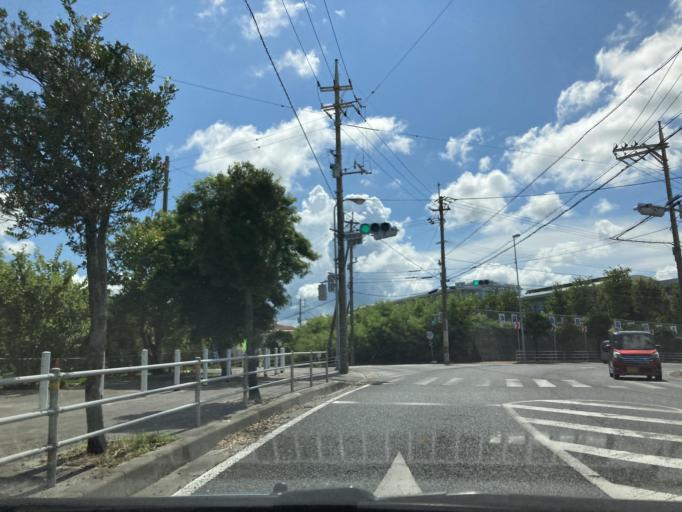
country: JP
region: Okinawa
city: Tomigusuku
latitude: 26.1721
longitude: 127.7219
